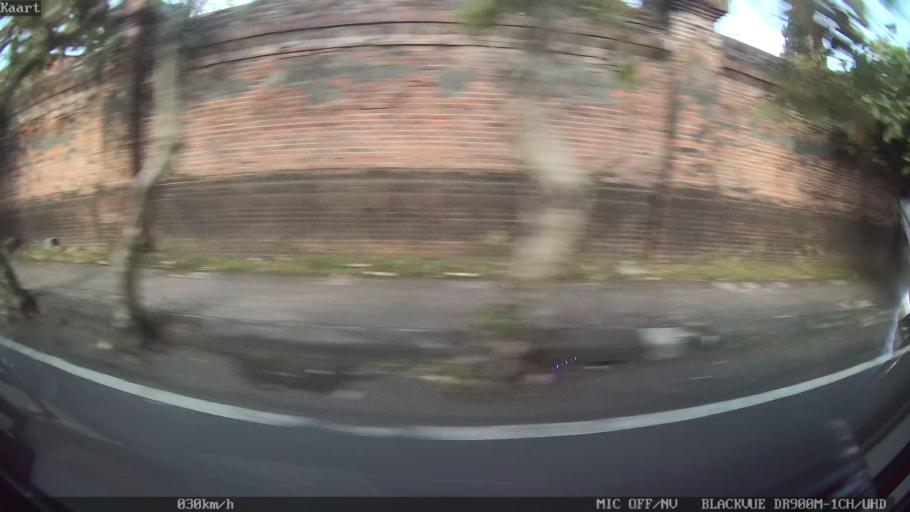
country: ID
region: Bali
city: Banjar Batur
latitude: -8.6115
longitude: 115.2132
